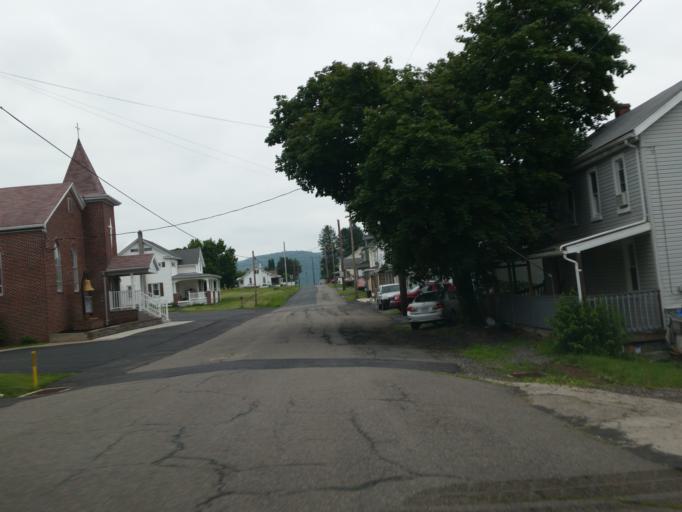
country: US
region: Pennsylvania
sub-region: Schuylkill County
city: Tower City
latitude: 40.5845
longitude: -76.5289
